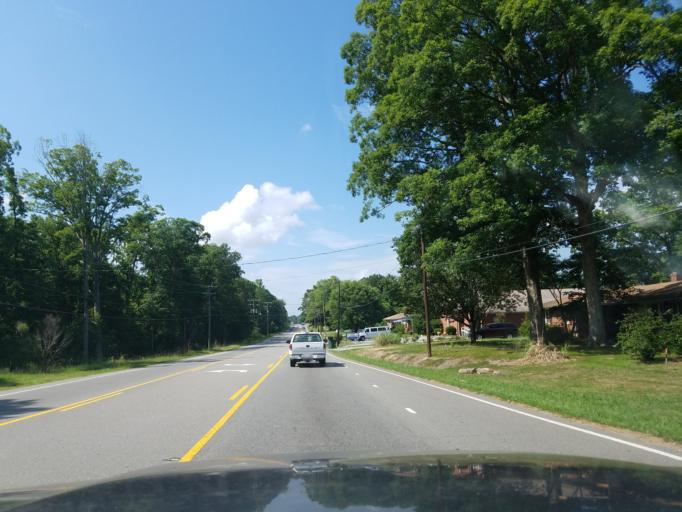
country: US
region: North Carolina
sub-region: Durham County
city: Durham
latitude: 35.9470
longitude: -78.9040
